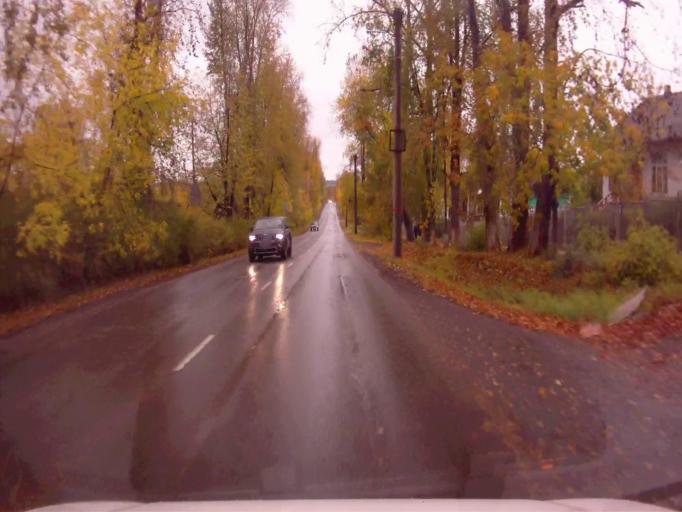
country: RU
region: Chelyabinsk
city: Verkhniy Ufaley
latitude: 56.0382
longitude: 60.2557
